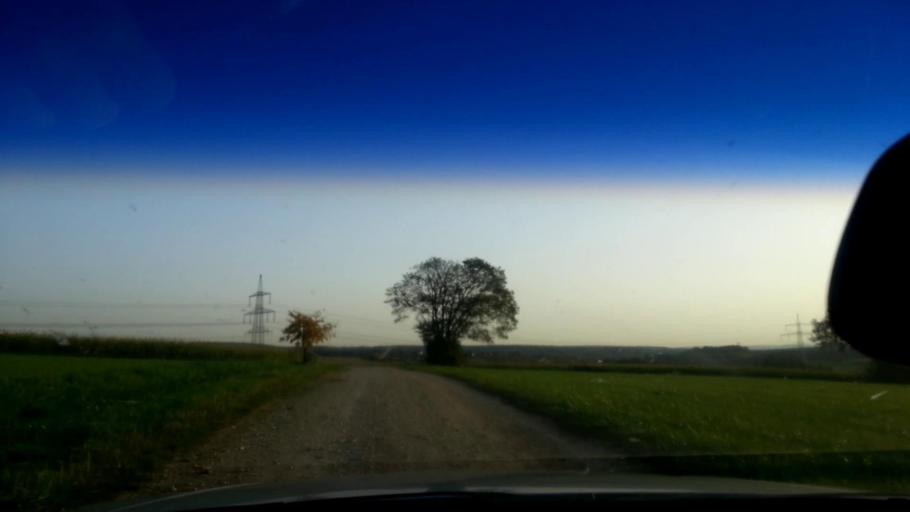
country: DE
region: Bavaria
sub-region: Upper Franconia
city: Memmelsdorf
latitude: 49.9579
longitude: 10.9701
